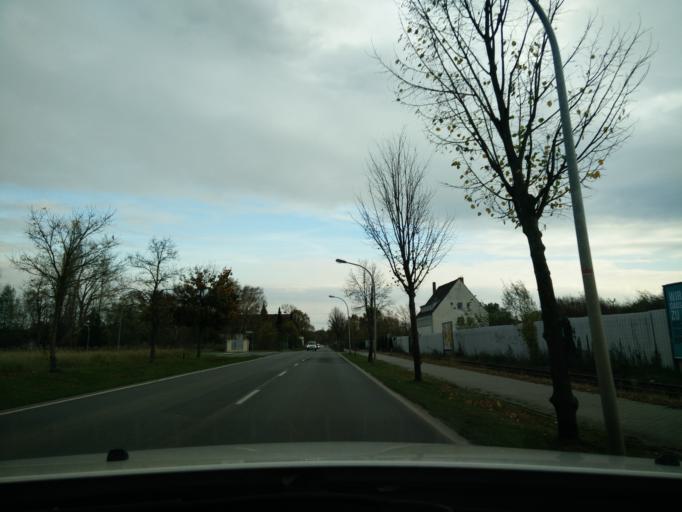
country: DE
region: Brandenburg
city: Velten
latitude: 52.6808
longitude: 13.1948
